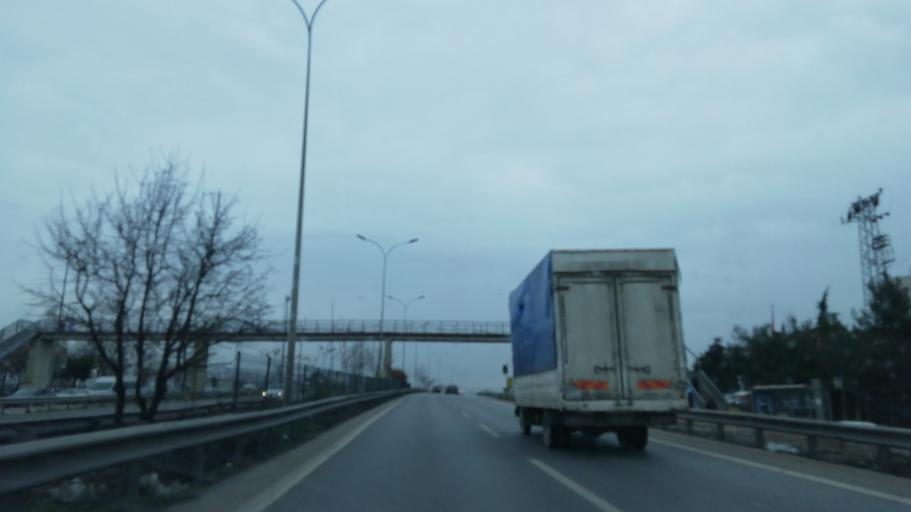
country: TR
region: Istanbul
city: Icmeler
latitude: 40.8231
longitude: 29.3529
